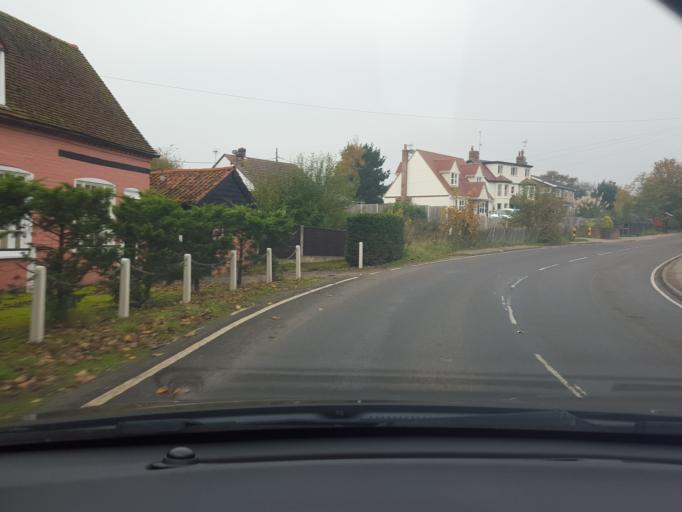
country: GB
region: England
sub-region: Essex
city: Alresford
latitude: 51.8935
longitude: 1.0273
